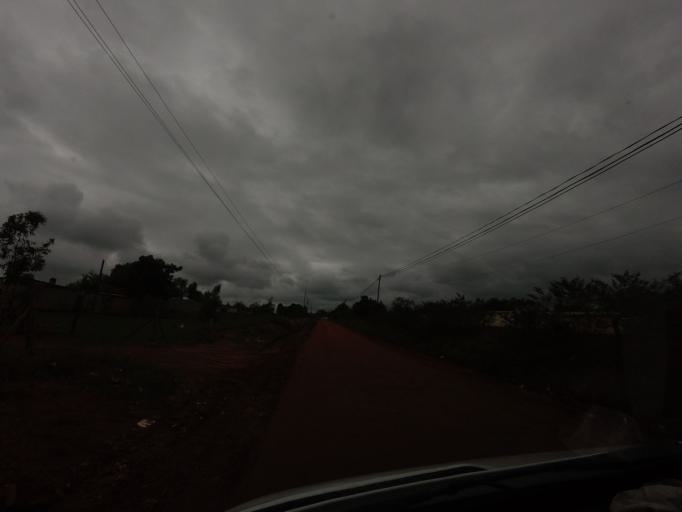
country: SZ
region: Hhohho
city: Lobamba
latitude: -26.4697
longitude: 31.2076
